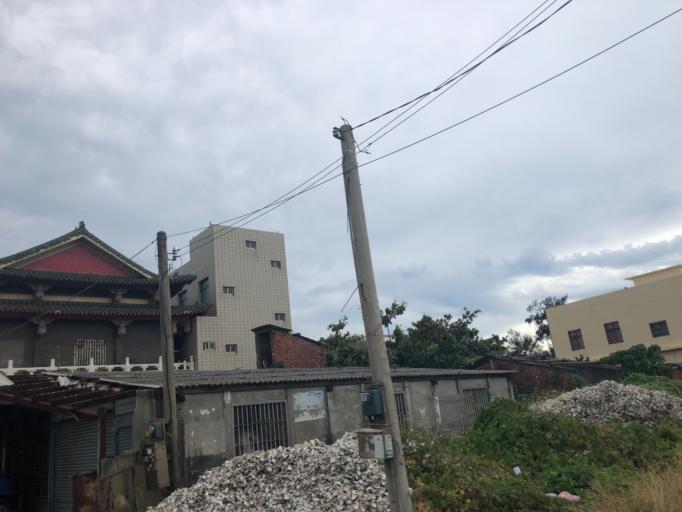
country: TW
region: Taiwan
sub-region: Chiayi
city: Taibao
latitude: 23.7058
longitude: 120.2004
